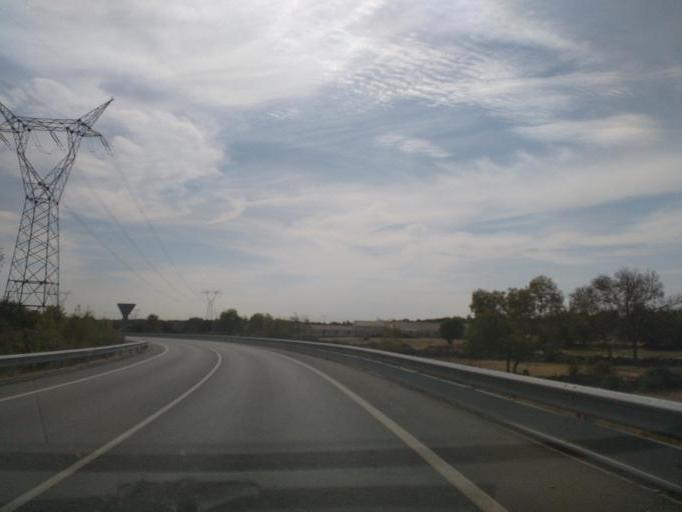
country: ES
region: Madrid
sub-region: Provincia de Madrid
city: Galapagar
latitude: 40.5816
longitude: -3.9972
